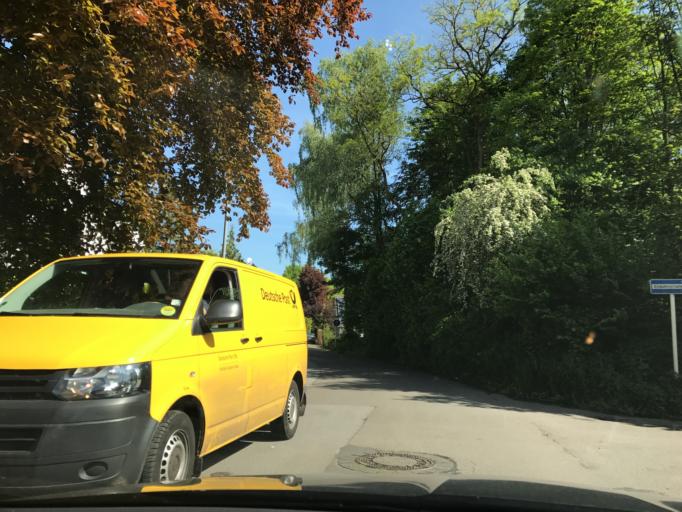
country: DE
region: North Rhine-Westphalia
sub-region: Regierungsbezirk Dusseldorf
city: Essen
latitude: 51.4214
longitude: 7.0530
